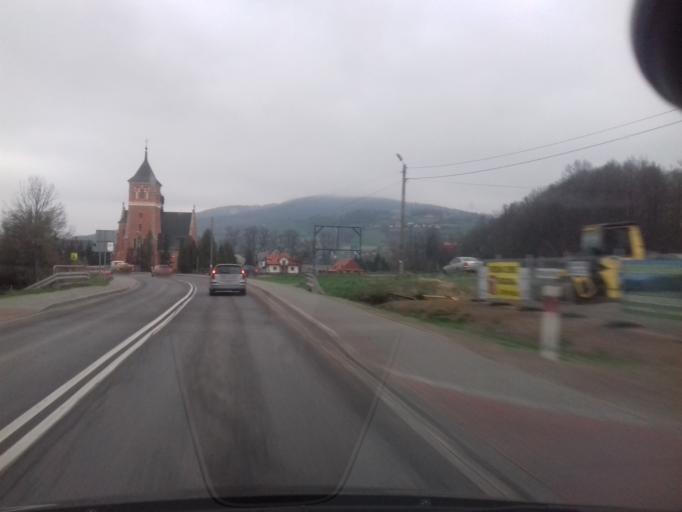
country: PL
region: Lesser Poland Voivodeship
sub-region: Powiat limanowski
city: Mszana Dolna
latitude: 49.7021
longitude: 20.0381
